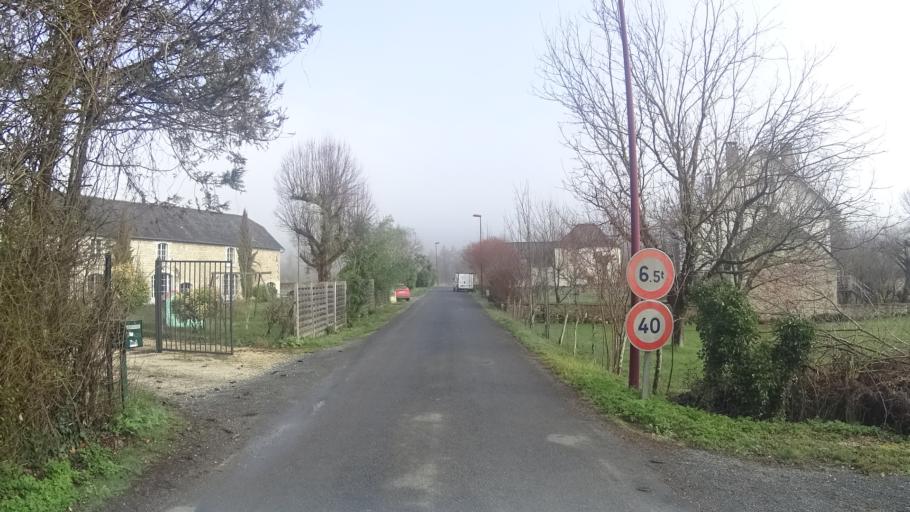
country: FR
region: Aquitaine
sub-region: Departement de la Dordogne
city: Terrasson-Lavilledieu
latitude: 45.0864
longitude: 1.2687
